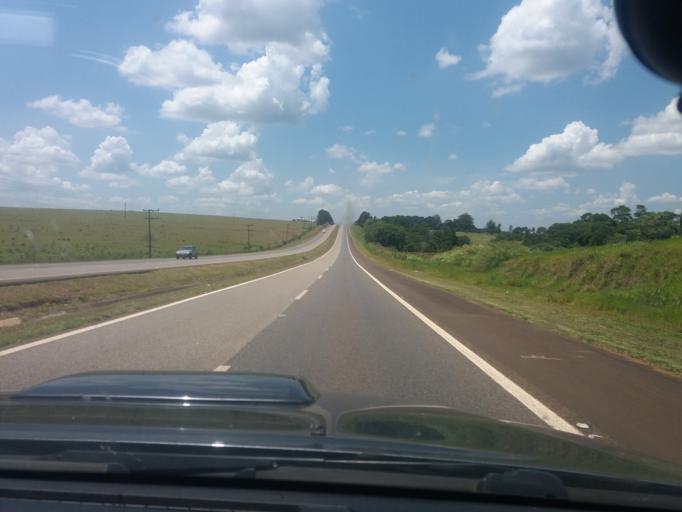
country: BR
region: Sao Paulo
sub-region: Itapetininga
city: Itapetininga
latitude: -23.5122
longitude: -47.9680
